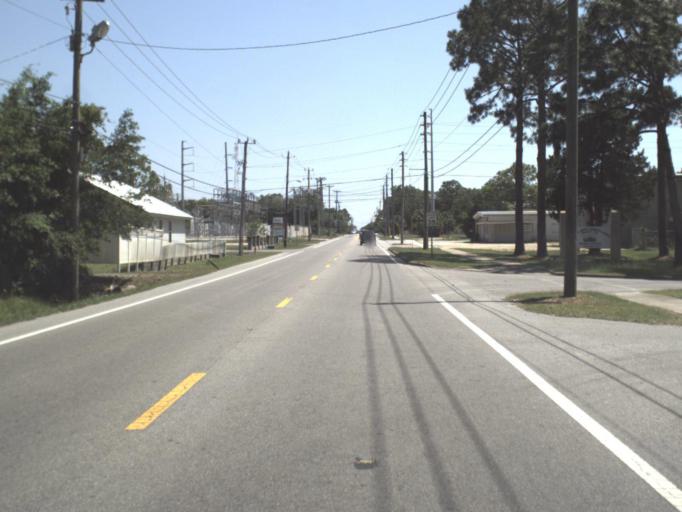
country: US
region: Florida
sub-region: Bay County
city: Pretty Bayou
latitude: 30.1866
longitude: -85.6836
